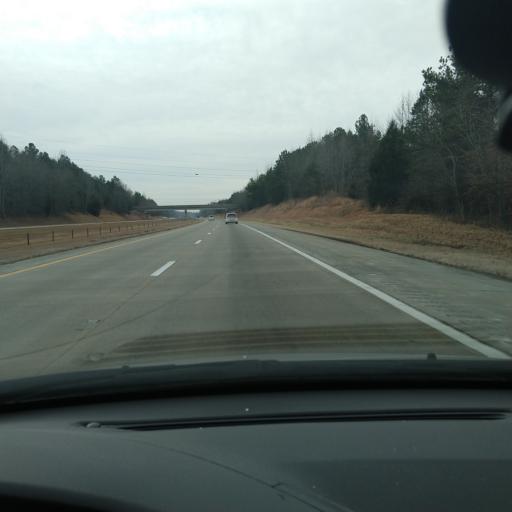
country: US
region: North Carolina
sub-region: Davidson County
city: Welcome
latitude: 35.9049
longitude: -80.2348
